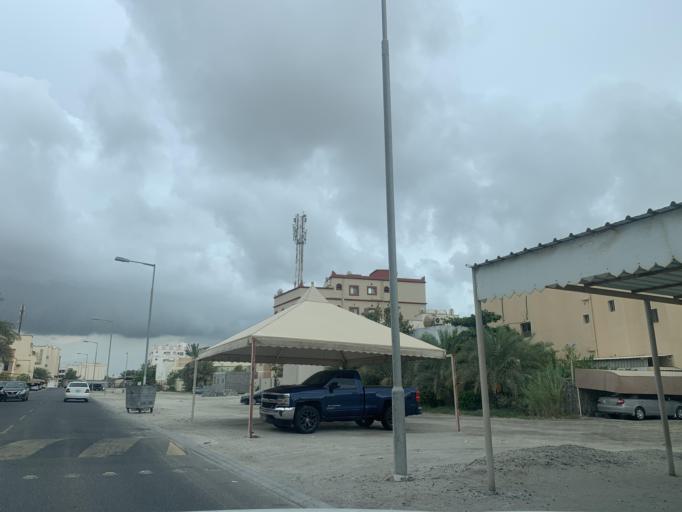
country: BH
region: Muharraq
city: Al Hadd
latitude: 26.2781
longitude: 50.6450
